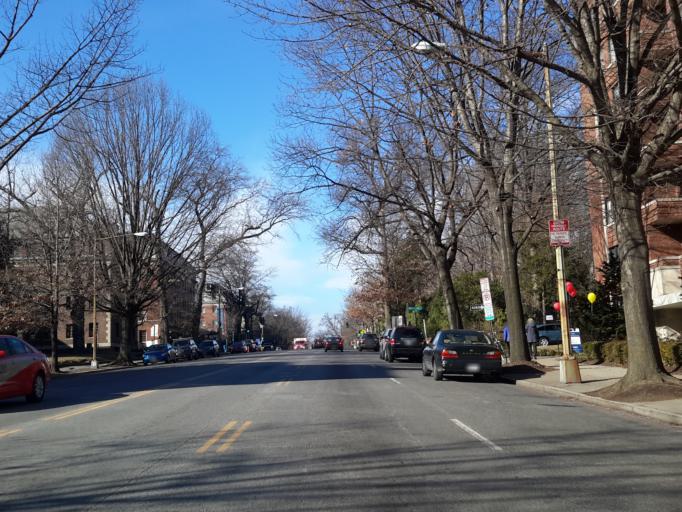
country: US
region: Washington, D.C.
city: Washington, D.C.
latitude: 38.9286
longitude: -77.0543
